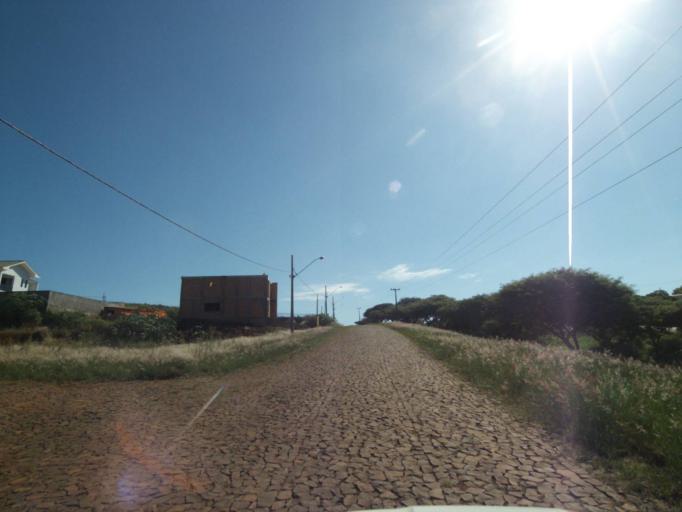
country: BR
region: Parana
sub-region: Laranjeiras Do Sul
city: Laranjeiras do Sul
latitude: -25.4875
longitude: -52.5257
